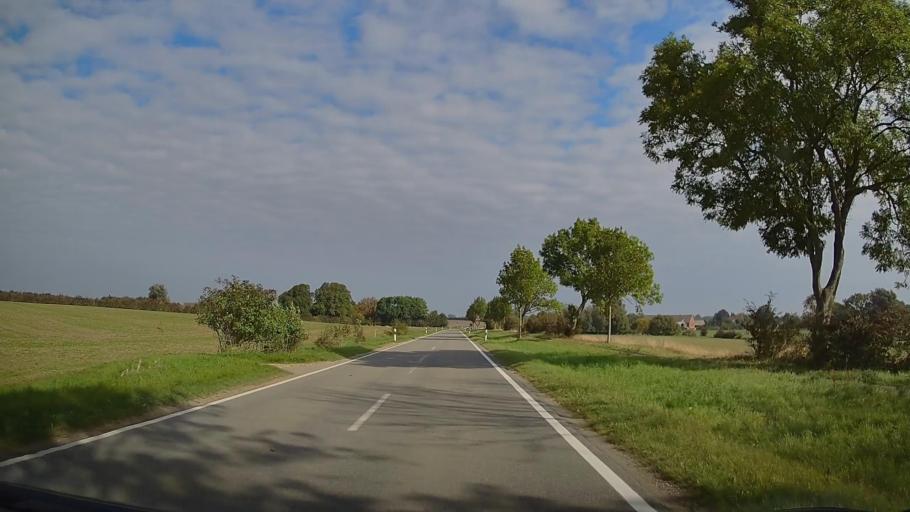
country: DE
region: Schleswig-Holstein
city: Gremersdorf
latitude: 54.3482
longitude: 10.9092
